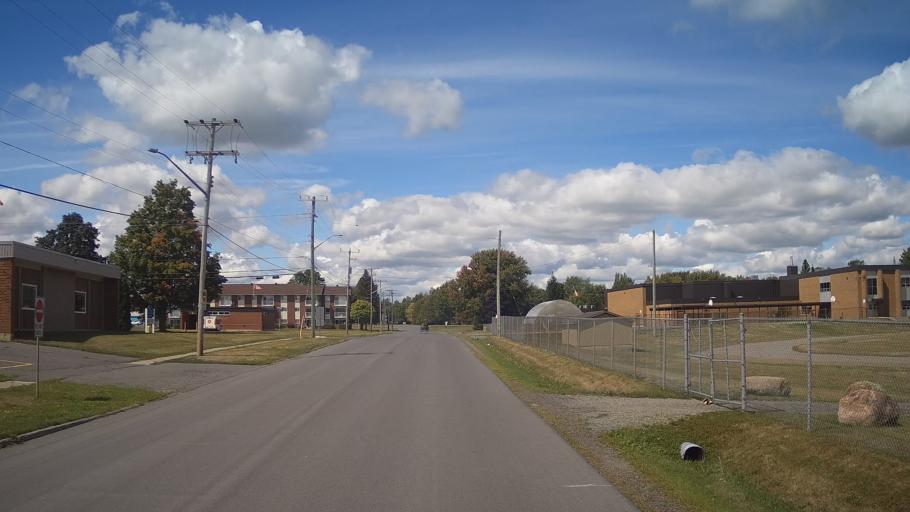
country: US
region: New York
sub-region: St. Lawrence County
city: Ogdensburg
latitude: 44.8491
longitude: -75.3141
